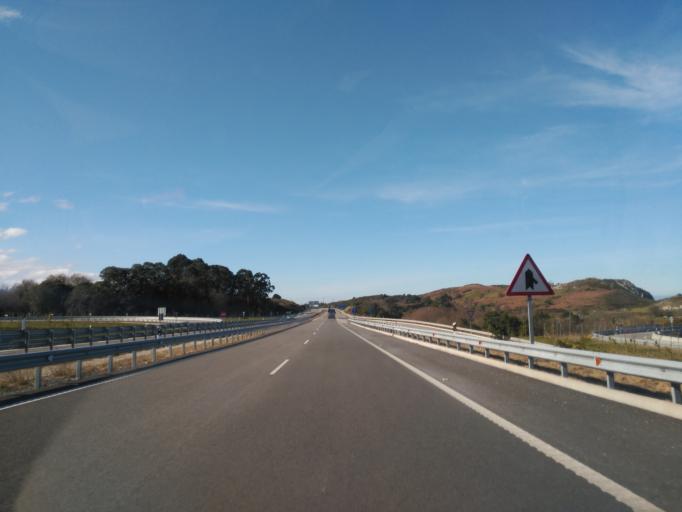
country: ES
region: Asturias
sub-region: Province of Asturias
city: Llanes
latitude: 43.3963
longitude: -4.6540
